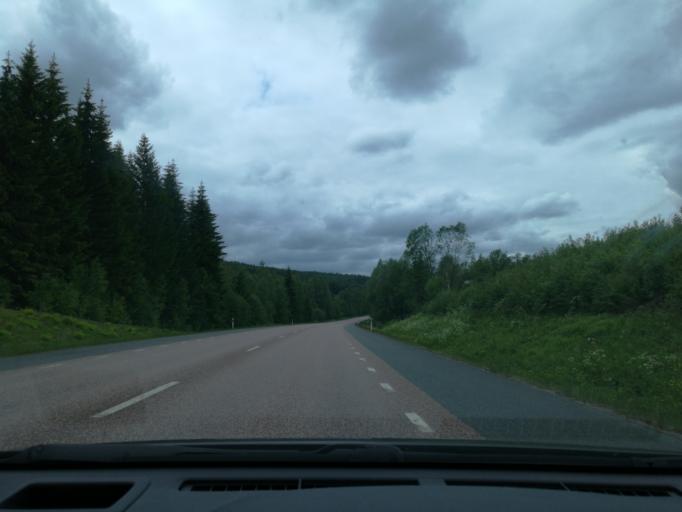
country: SE
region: Vaestmanland
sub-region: Fagersta Kommun
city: Fagersta
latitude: 59.9661
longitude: 15.7323
